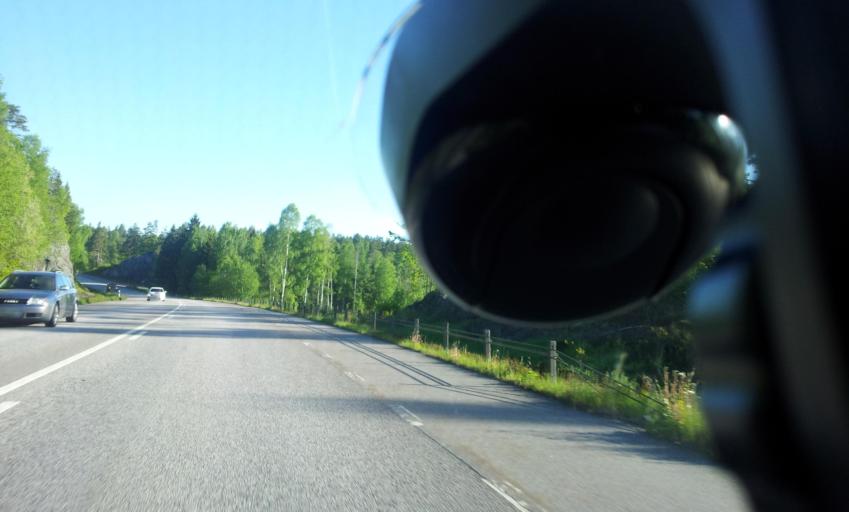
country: SE
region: Kalmar
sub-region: Vasterviks Kommun
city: Ankarsrum
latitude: 57.6284
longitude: 16.4591
